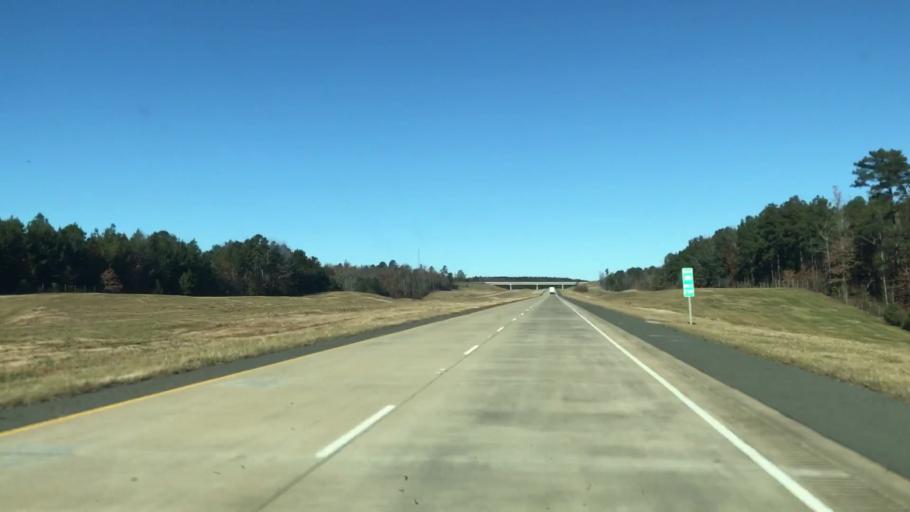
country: US
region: Louisiana
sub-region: Caddo Parish
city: Vivian
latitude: 32.9165
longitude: -93.8784
